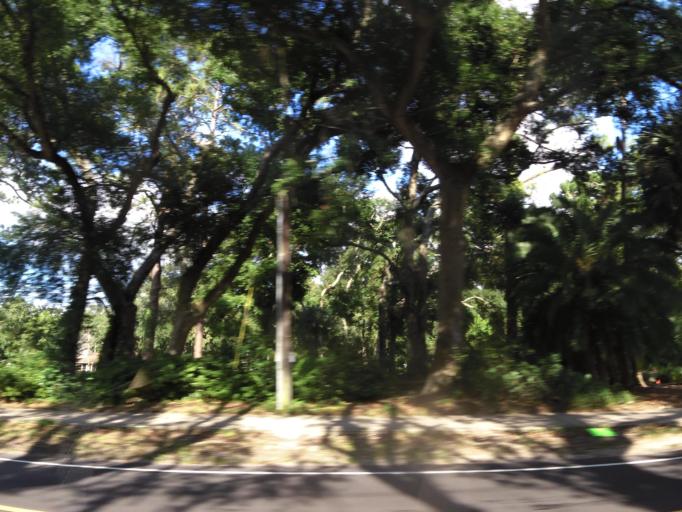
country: US
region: Georgia
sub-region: Glynn County
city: Saint Simon Mills
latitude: 31.1894
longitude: -81.3768
